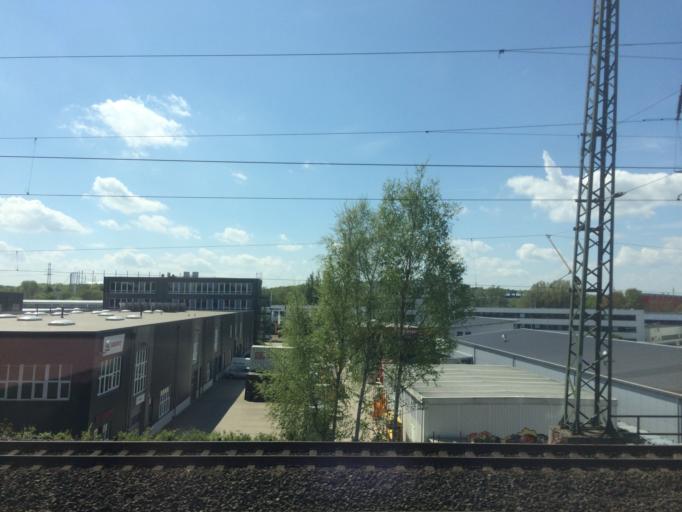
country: DE
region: Hamburg
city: Eidelstedt
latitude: 53.5971
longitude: 9.9045
